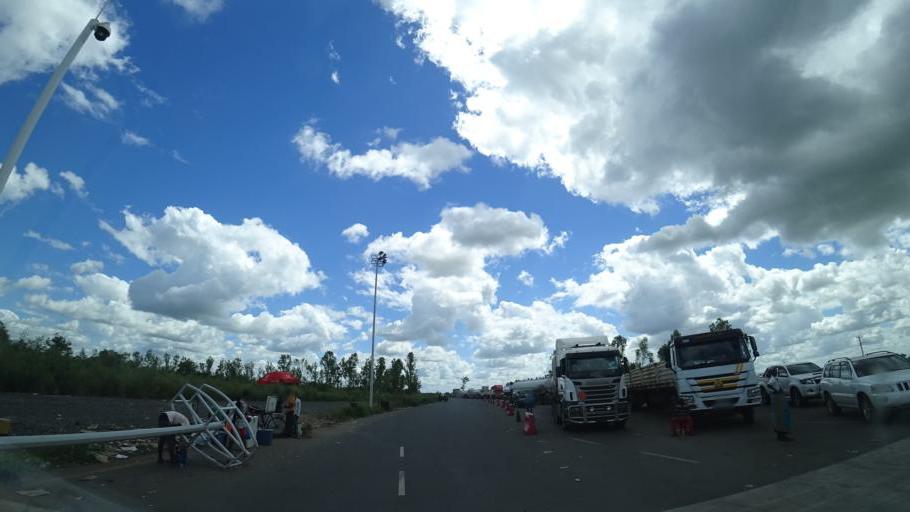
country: MZ
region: Sofala
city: Dondo
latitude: -19.2861
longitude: 34.2260
